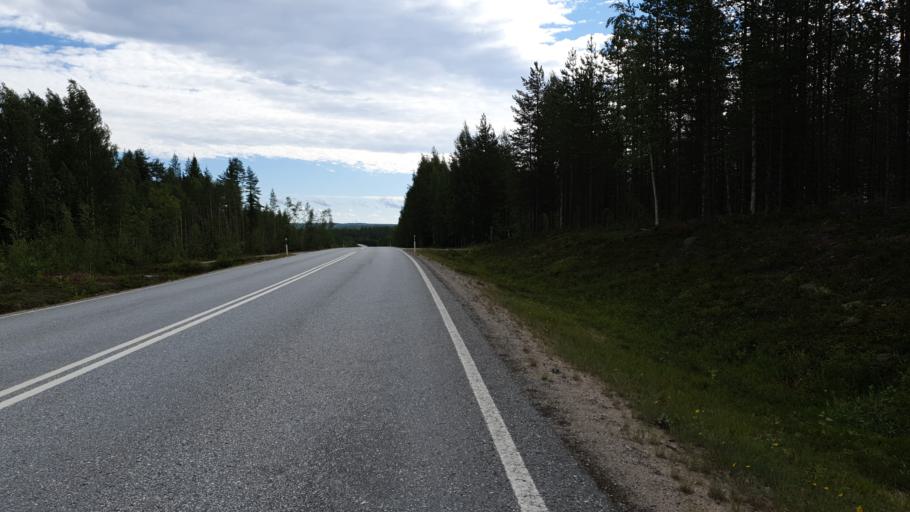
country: FI
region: Kainuu
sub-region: Kehys-Kainuu
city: Kuhmo
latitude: 64.4902
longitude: 29.8603
